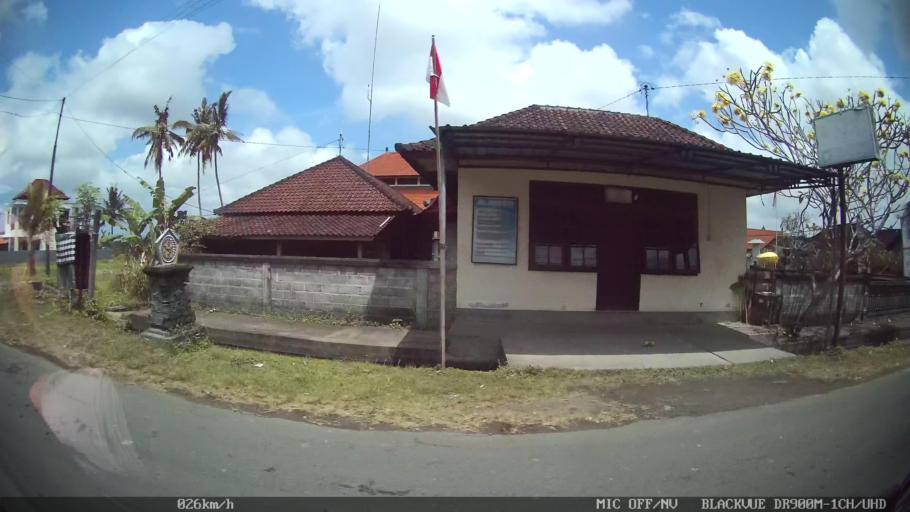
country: ID
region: Bali
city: Banjar Desa
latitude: -8.5767
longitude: 115.2869
